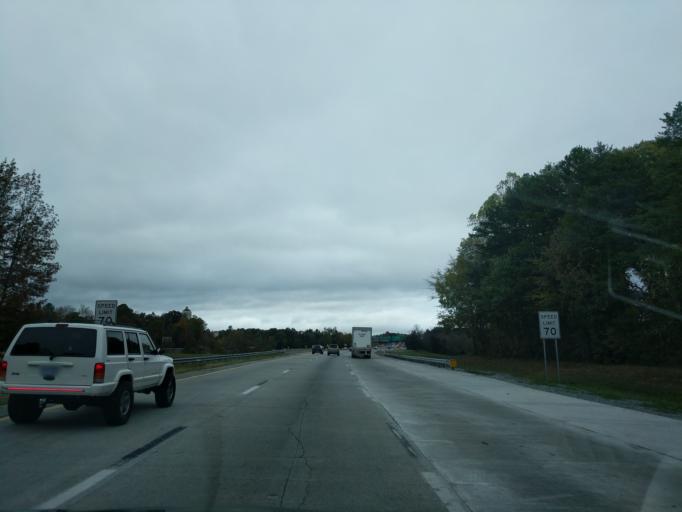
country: US
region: North Carolina
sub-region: Guilford County
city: Jamestown
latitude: 35.9836
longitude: -79.8854
